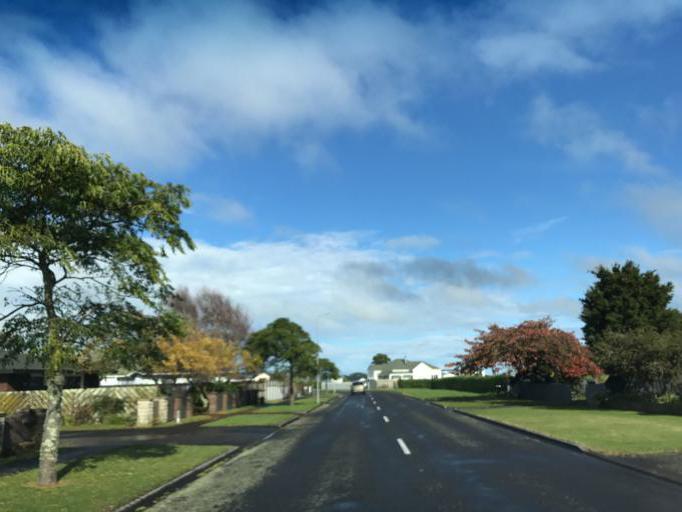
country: NZ
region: Taranaki
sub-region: South Taranaki District
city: Hawera
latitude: -39.5717
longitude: 174.2673
